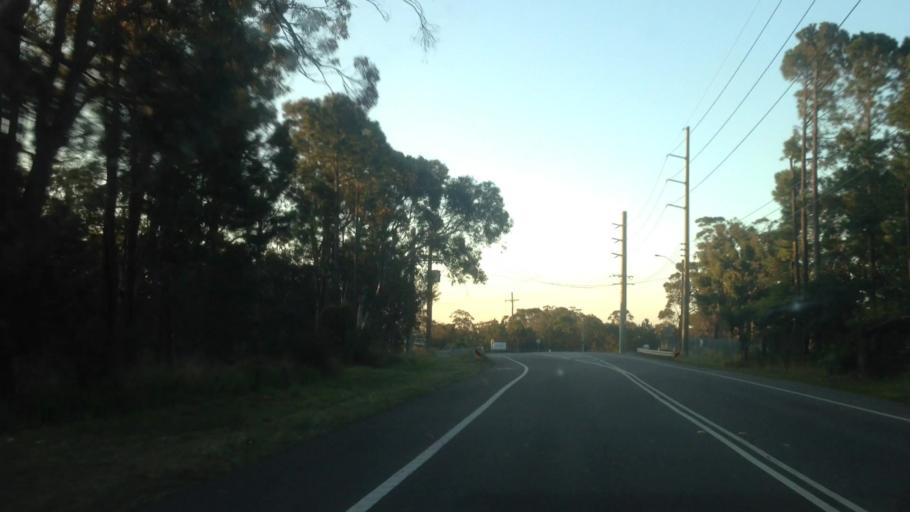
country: AU
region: New South Wales
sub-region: Wyong Shire
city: Kingfisher Shores
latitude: -33.1745
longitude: 151.5396
